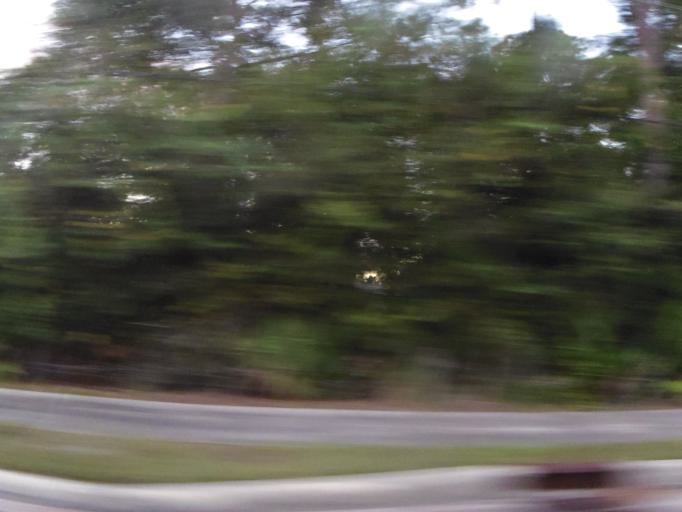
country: US
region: Florida
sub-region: Saint Johns County
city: Palm Valley
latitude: 30.0890
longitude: -81.4604
